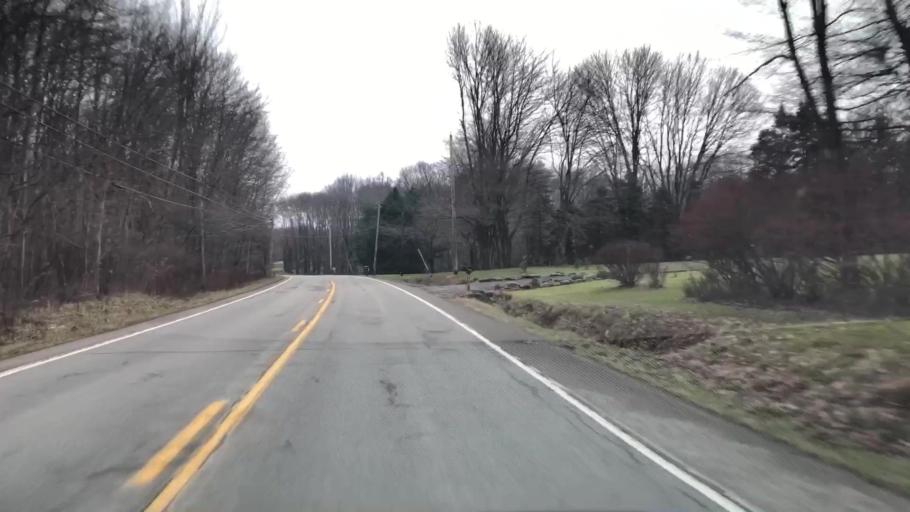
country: US
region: Pennsylvania
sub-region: Mercer County
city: Grove City
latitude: 41.1263
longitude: -80.0702
